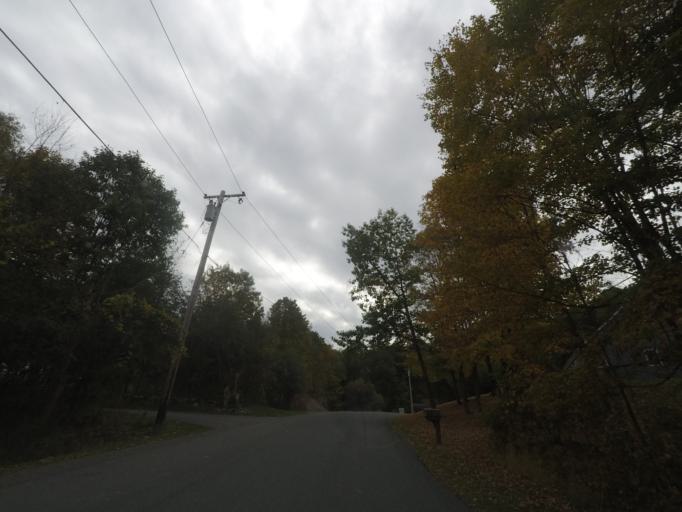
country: US
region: New York
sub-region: Rensselaer County
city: Nassau
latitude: 42.5452
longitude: -73.6451
